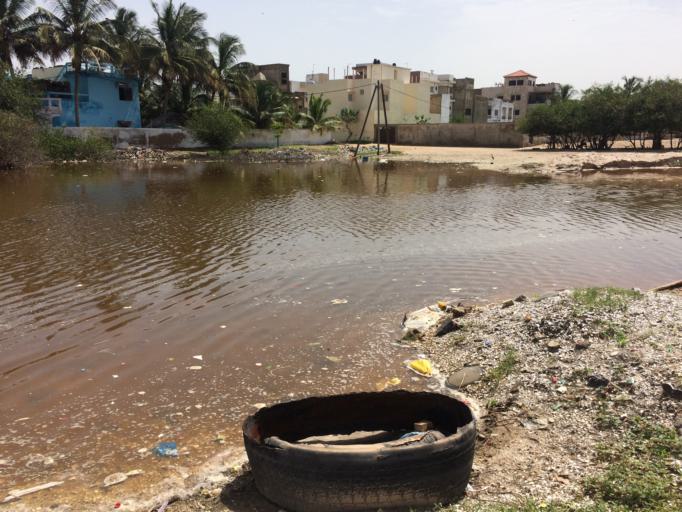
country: SN
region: Dakar
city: Pikine
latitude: 14.7305
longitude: -17.3291
